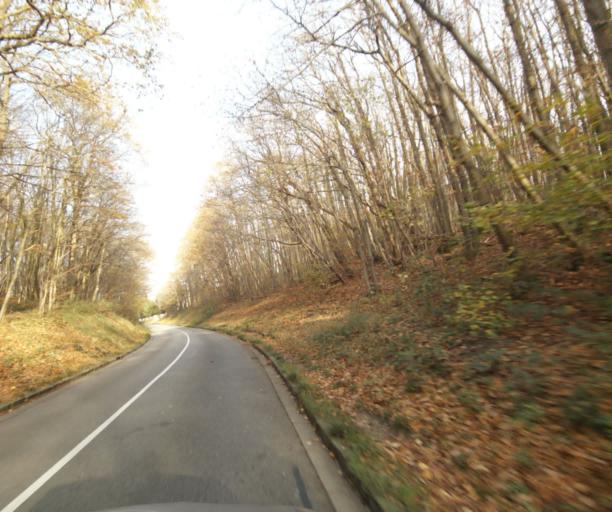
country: FR
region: Ile-de-France
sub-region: Departement des Yvelines
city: Triel-sur-Seine
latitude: 48.9968
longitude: 2.0074
